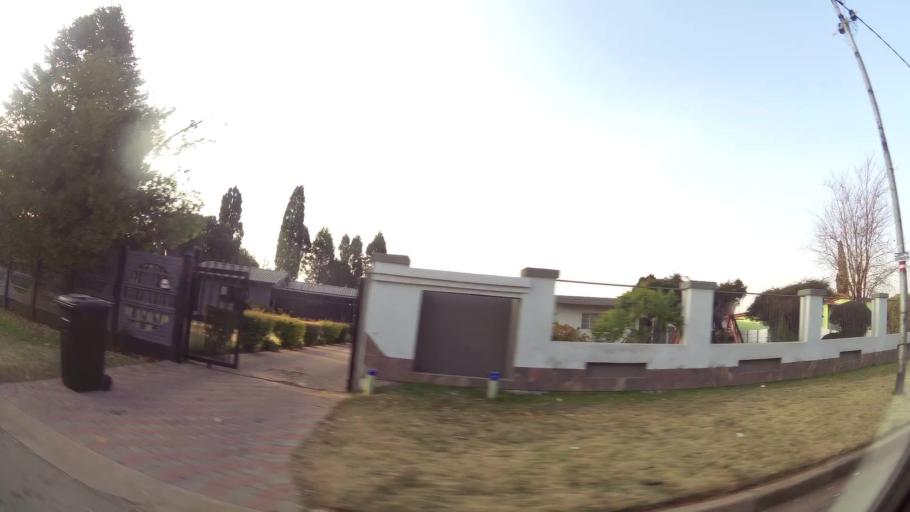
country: ZA
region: Gauteng
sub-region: Ekurhuleni Metropolitan Municipality
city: Springs
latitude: -26.2624
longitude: 28.4017
